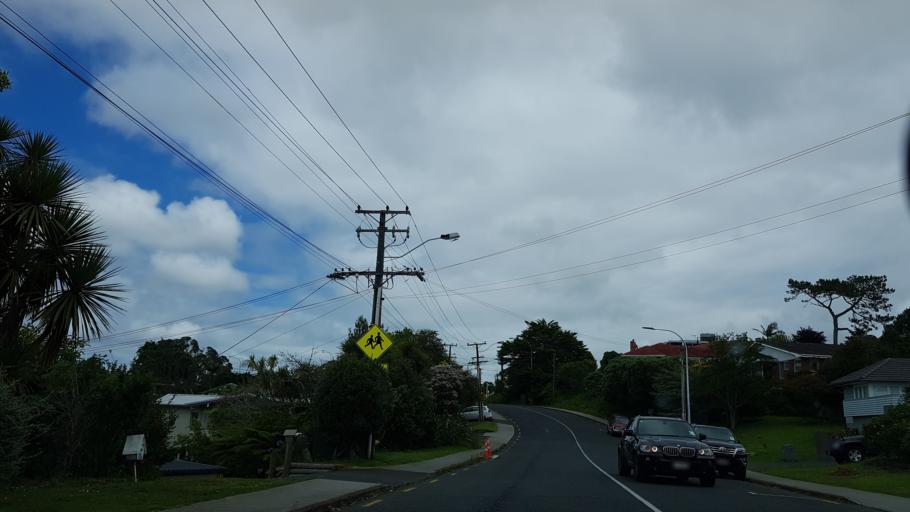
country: NZ
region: Auckland
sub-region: Auckland
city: Rothesay Bay
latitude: -36.7358
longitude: 174.7388
